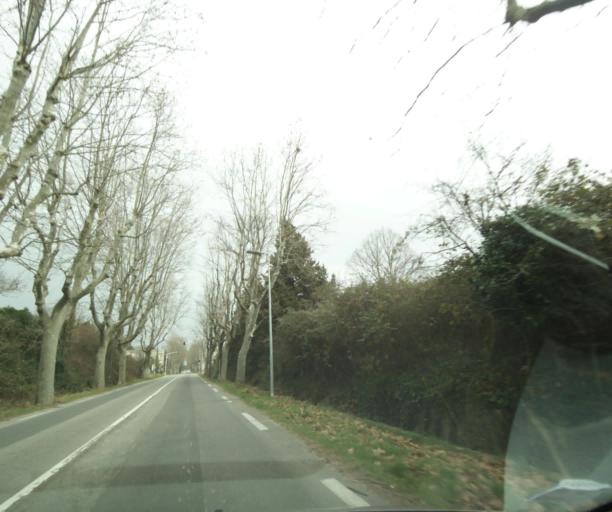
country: FR
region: Provence-Alpes-Cote d'Azur
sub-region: Departement des Bouches-du-Rhone
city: Aix-en-Provence
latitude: 43.5607
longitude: 5.4622
